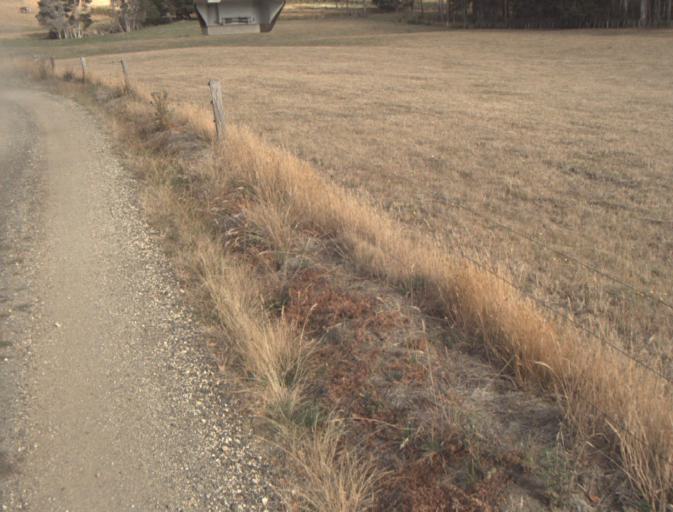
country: AU
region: Tasmania
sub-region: Dorset
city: Bridport
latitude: -41.1253
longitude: 147.2041
